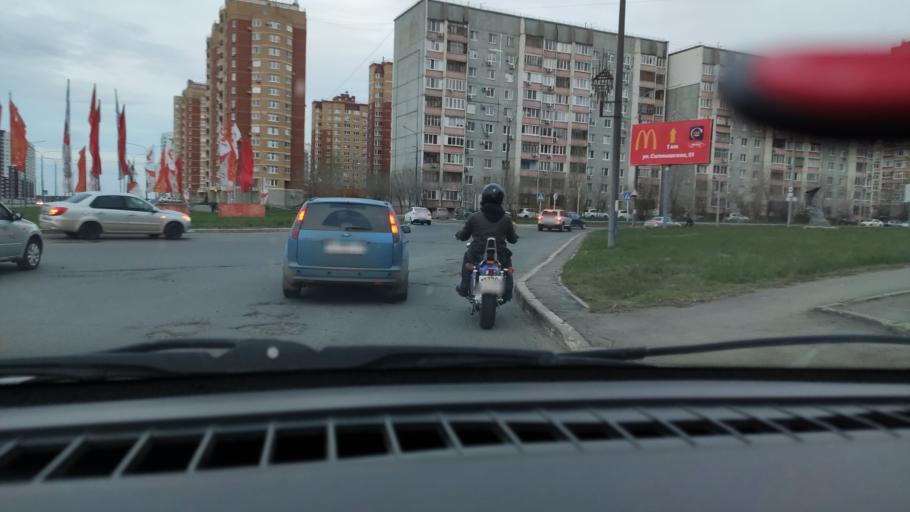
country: RU
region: Orenburg
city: Orenburg
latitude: 51.8238
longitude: 55.1651
